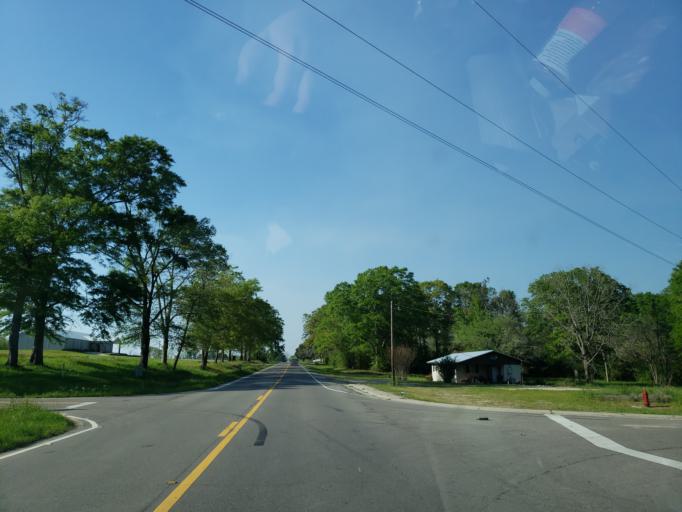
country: US
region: Mississippi
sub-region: Perry County
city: Richton
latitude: 31.3823
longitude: -88.9368
